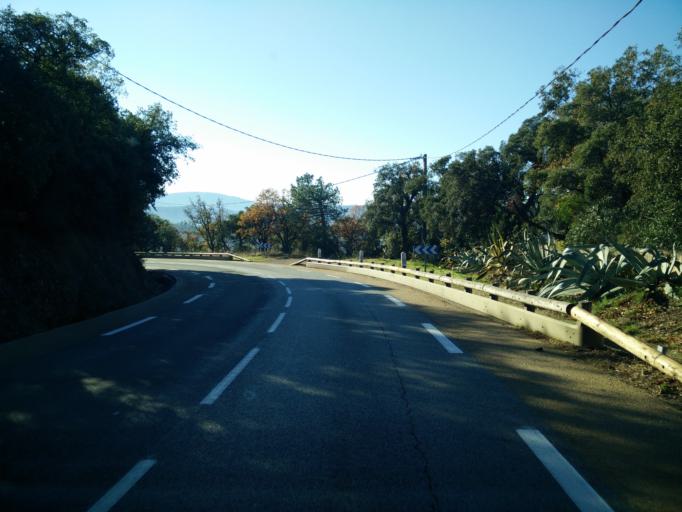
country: FR
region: Provence-Alpes-Cote d'Azur
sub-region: Departement du Var
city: Grimaud
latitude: 43.2740
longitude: 6.5098
